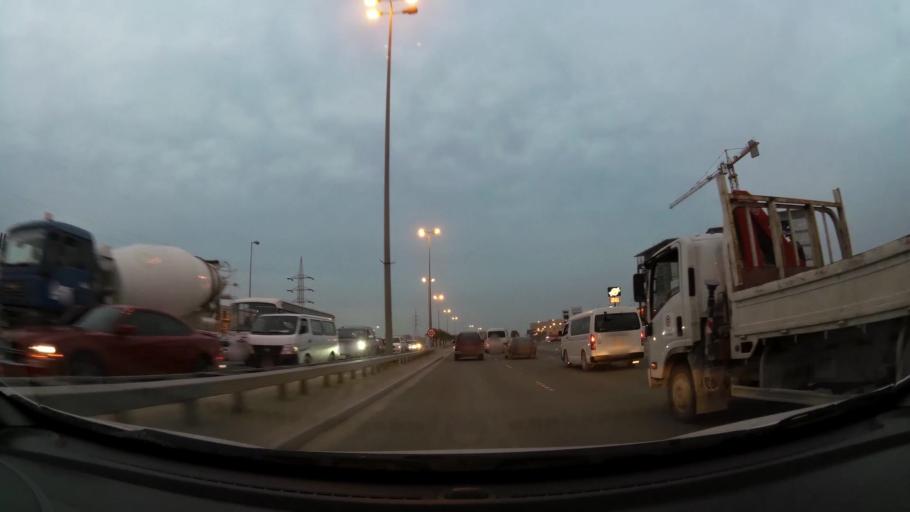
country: BH
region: Northern
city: Ar Rifa'
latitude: 26.1420
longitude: 50.5800
